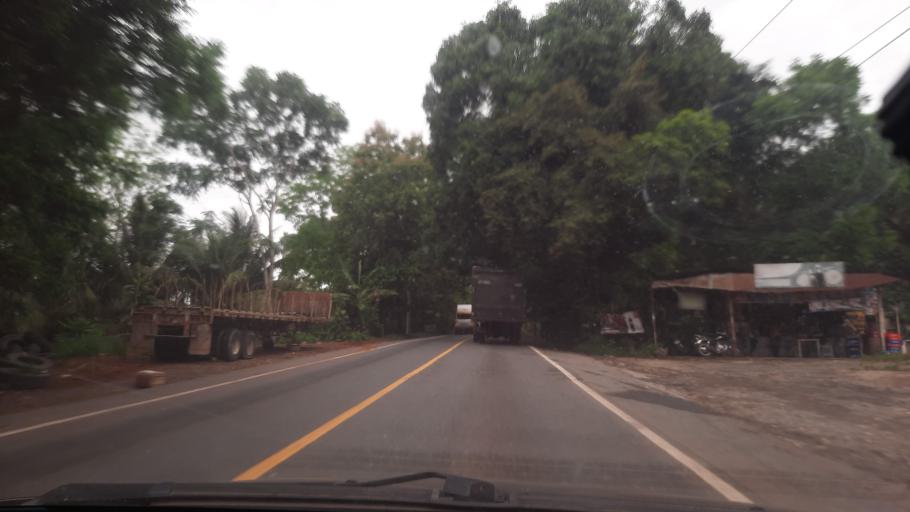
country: GT
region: Izabal
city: Morales
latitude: 15.4626
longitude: -88.9263
